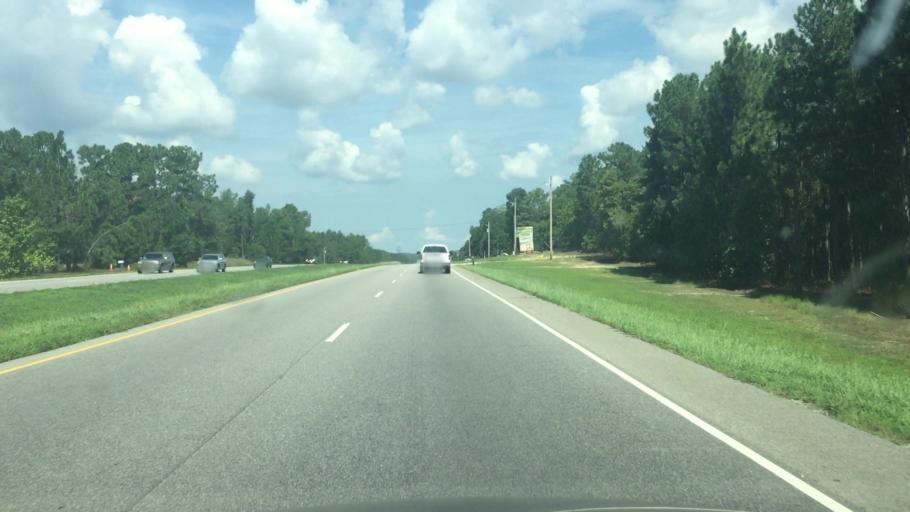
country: US
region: North Carolina
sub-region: Scotland County
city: Laurel Hill
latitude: 34.8406
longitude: -79.6029
